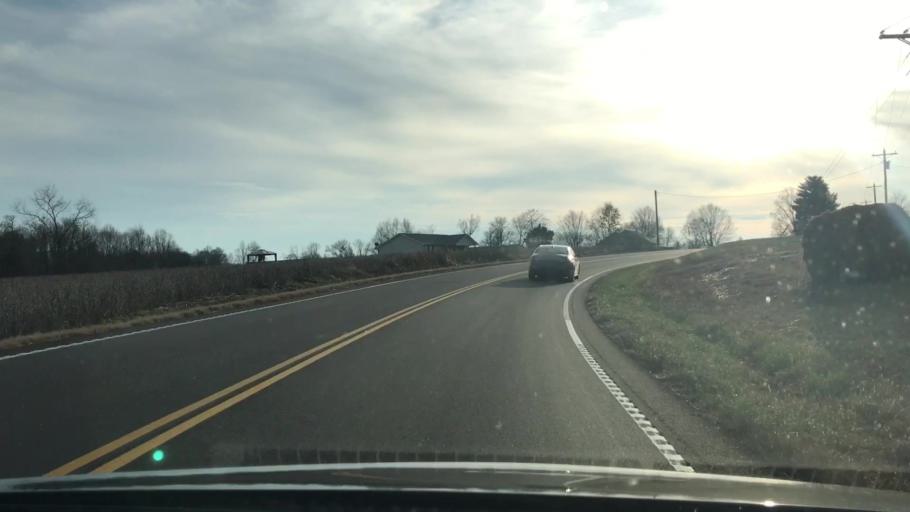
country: US
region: Tennessee
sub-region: Macon County
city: Red Boiling Springs
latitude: 36.5068
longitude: -85.8623
